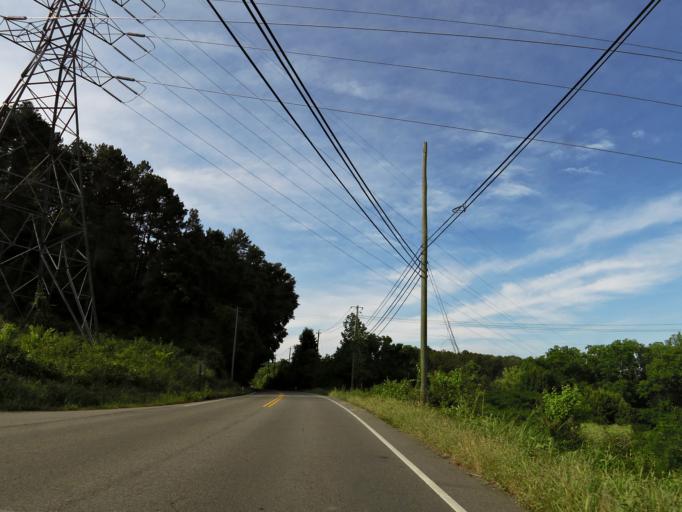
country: US
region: Tennessee
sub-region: Blount County
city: Eagleton Village
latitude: 35.8688
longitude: -83.9439
